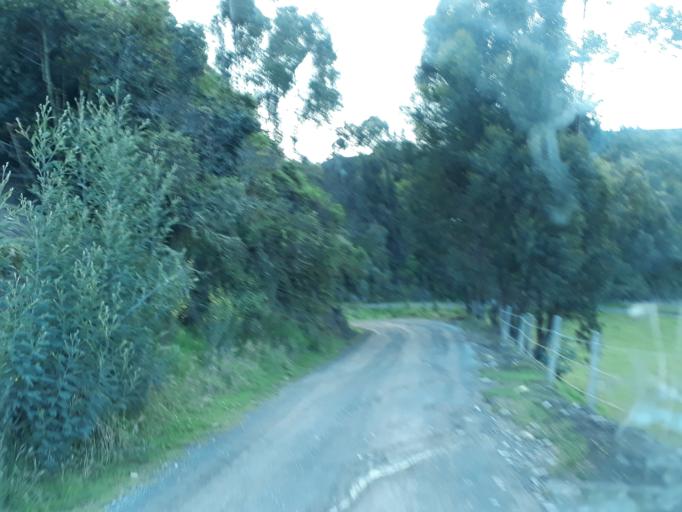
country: CO
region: Cundinamarca
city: Carmen de Carupa
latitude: 5.3373
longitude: -73.9076
